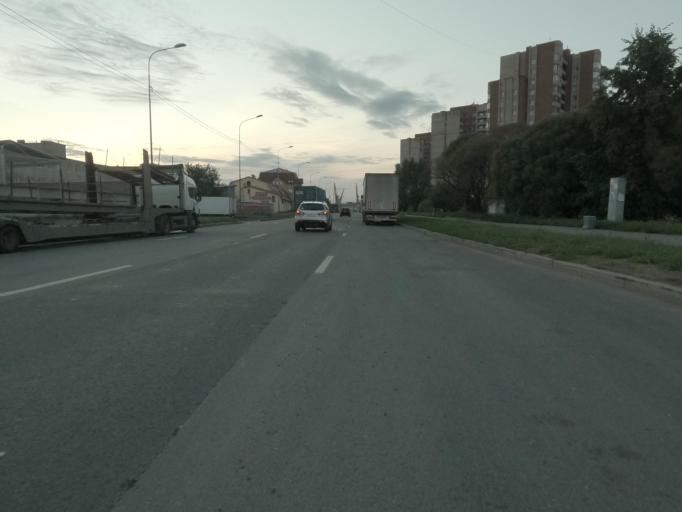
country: RU
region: St.-Petersburg
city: Vasyl'evsky Ostrov
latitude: 59.9055
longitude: 30.2453
